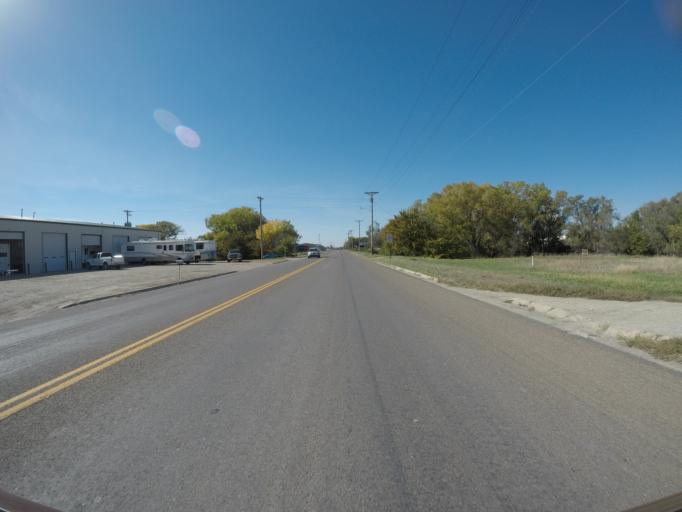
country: US
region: Kansas
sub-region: Smith County
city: Smith Center
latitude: 39.7852
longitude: -98.7778
